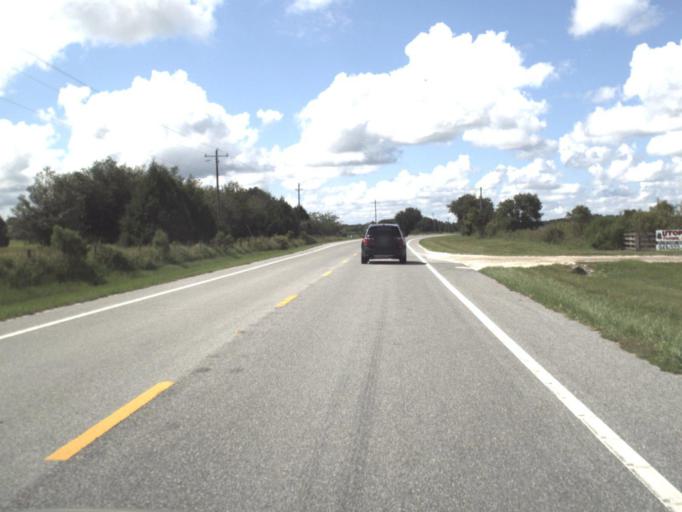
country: US
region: Florida
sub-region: DeSoto County
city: Arcadia
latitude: 27.3104
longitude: -82.1005
